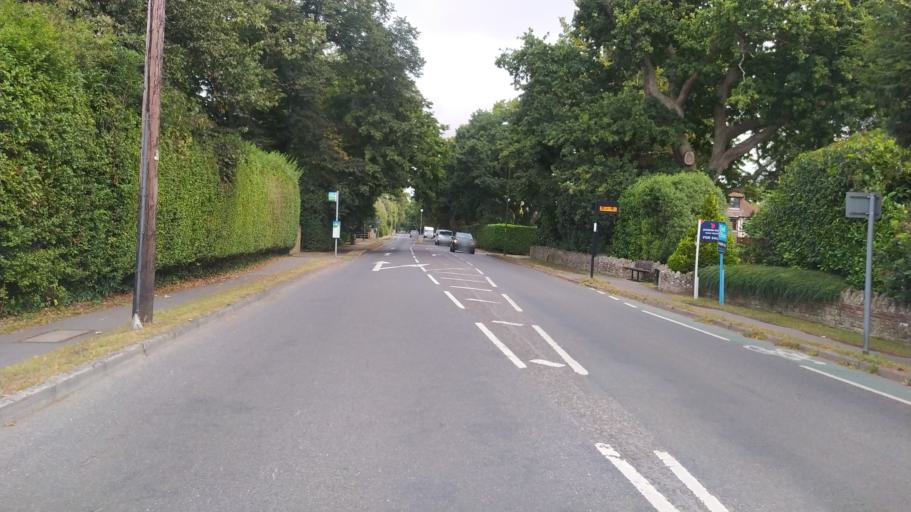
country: GB
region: England
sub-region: West Sussex
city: Chichester
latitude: 50.8544
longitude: -0.7819
